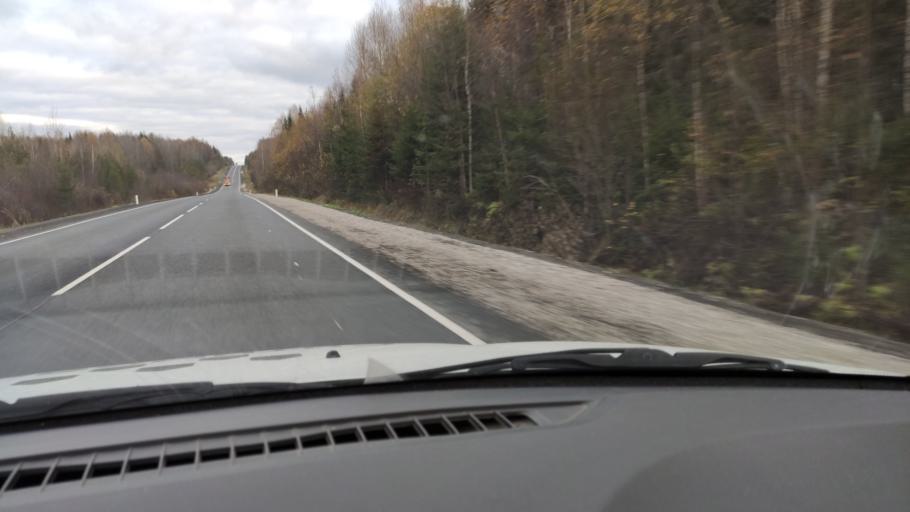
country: RU
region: Kirov
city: Chernaya Kholunitsa
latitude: 58.8896
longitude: 51.3612
